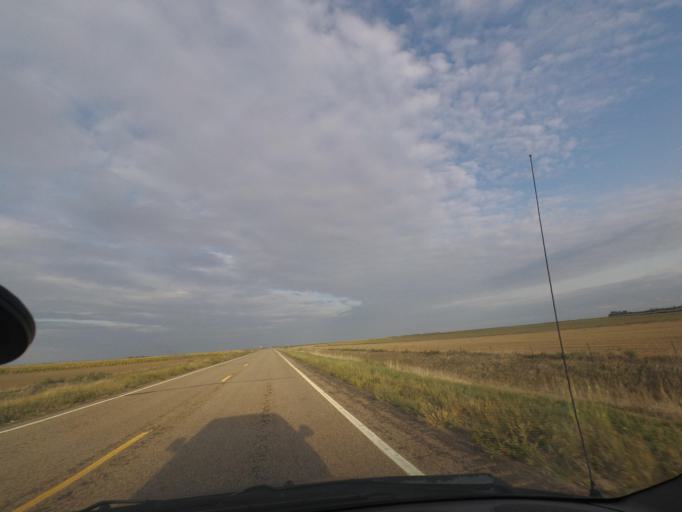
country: US
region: Colorado
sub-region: Yuma County
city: Wray
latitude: 39.7017
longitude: -102.3767
